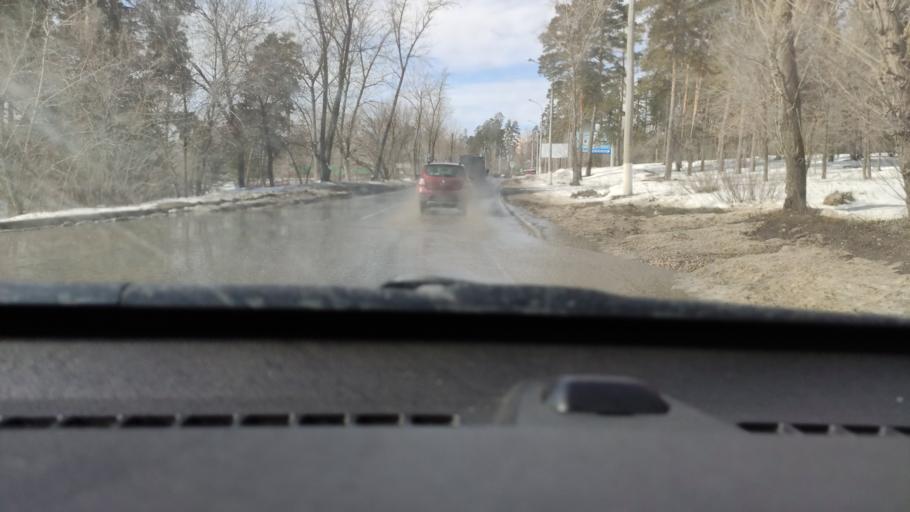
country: RU
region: Samara
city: Tol'yatti
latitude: 53.4745
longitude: 49.3801
